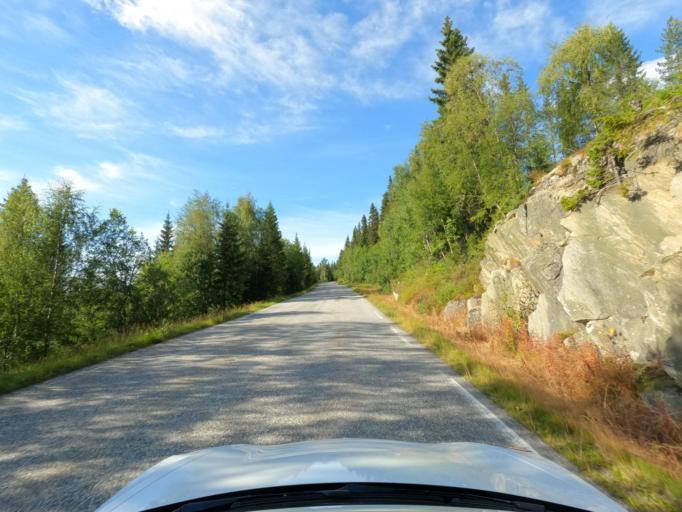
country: NO
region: Telemark
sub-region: Hjartdal
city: Sauland
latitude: 59.9158
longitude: 8.9914
